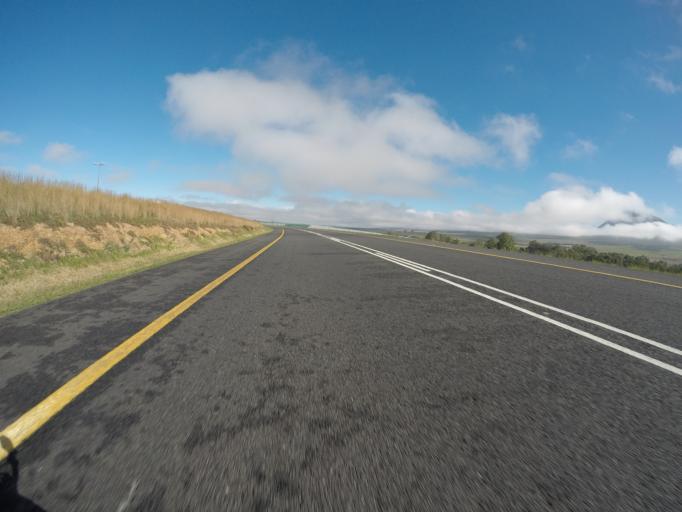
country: ZA
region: Western Cape
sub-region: Cape Winelands District Municipality
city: Ashton
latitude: -34.1182
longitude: 20.0438
